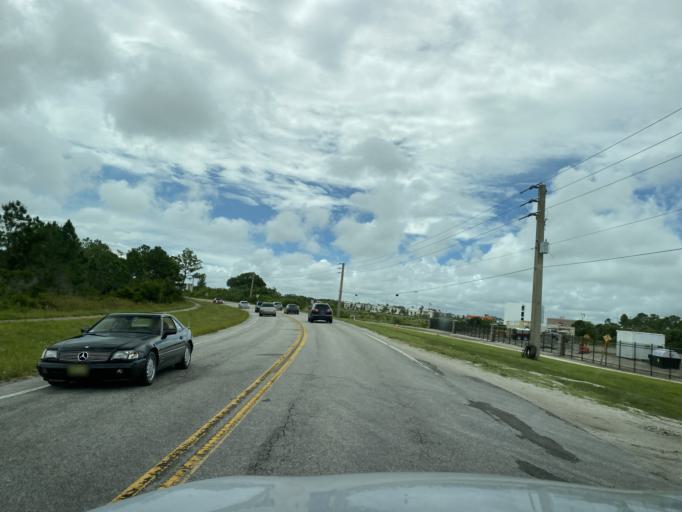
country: US
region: Florida
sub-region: Brevard County
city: West Melbourne
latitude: 28.0411
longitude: -80.6542
